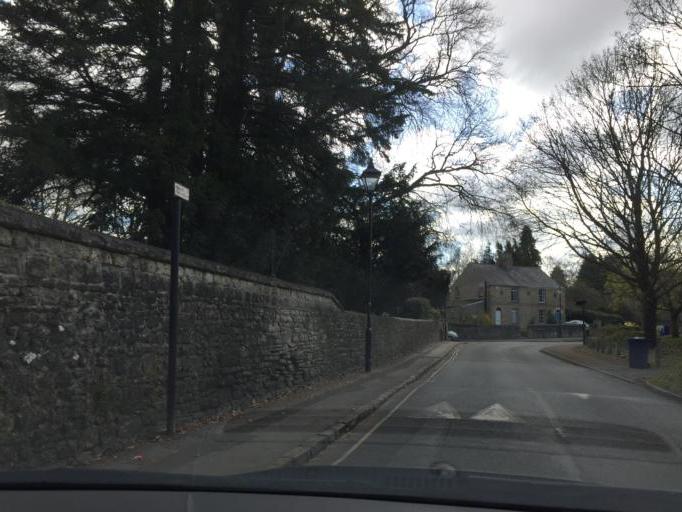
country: GB
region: England
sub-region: Oxfordshire
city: Cowley
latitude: 51.7656
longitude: -1.2148
